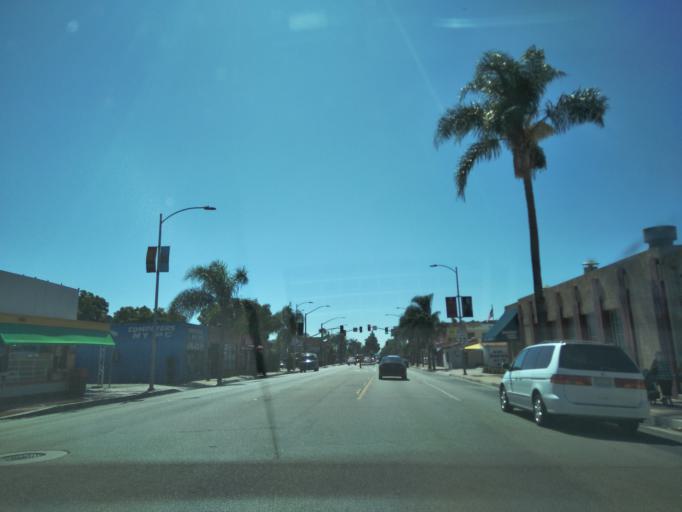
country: US
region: California
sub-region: Orange County
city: Santa Ana
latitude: 33.7264
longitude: -117.8679
